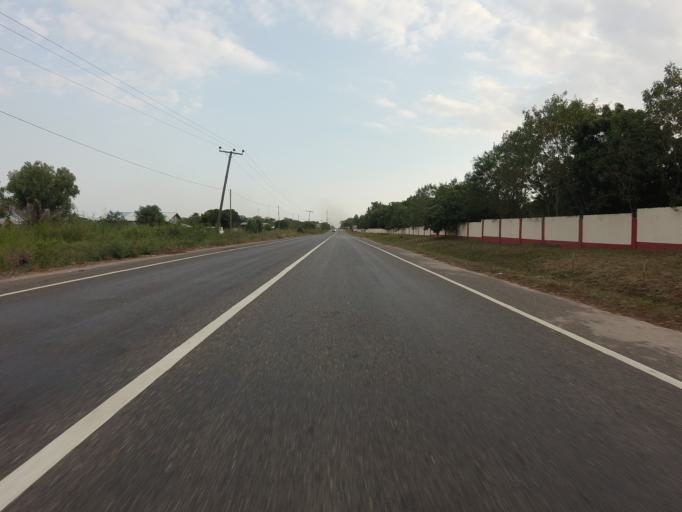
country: GH
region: Volta
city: Anloga
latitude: 6.0952
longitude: 0.5082
